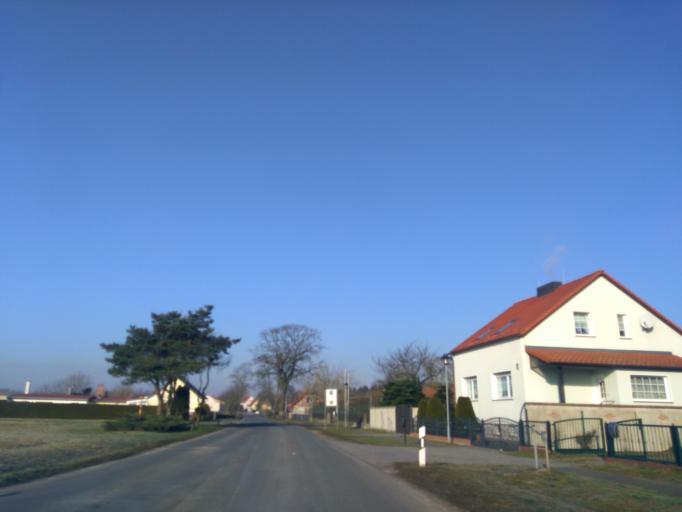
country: DE
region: Brandenburg
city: Brieselang
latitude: 52.6510
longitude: 12.9949
